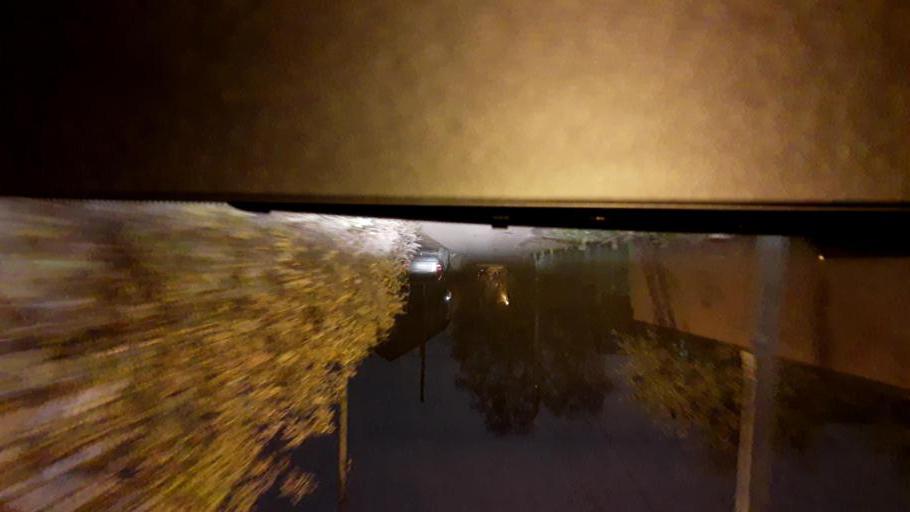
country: RU
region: Nizjnij Novgorod
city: Nizhniy Novgorod
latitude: 56.3062
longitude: 43.9245
